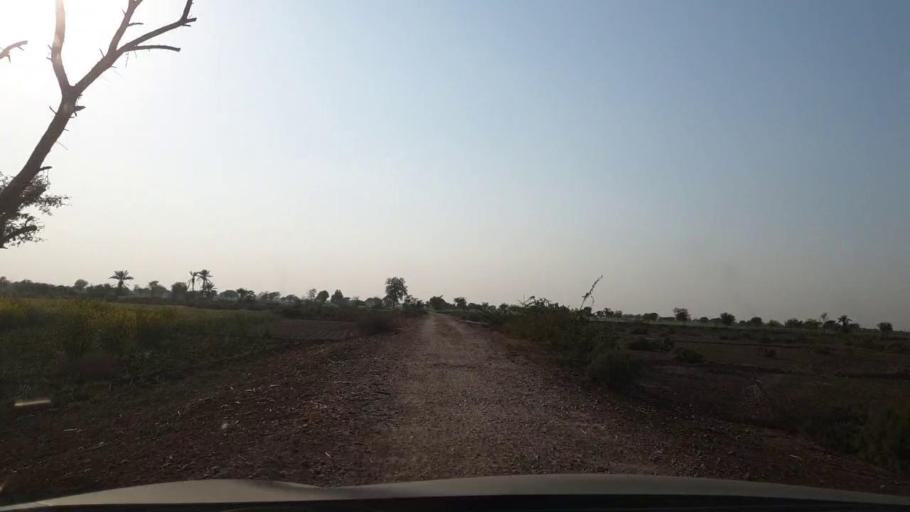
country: PK
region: Sindh
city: Berani
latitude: 25.6543
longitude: 68.8144
